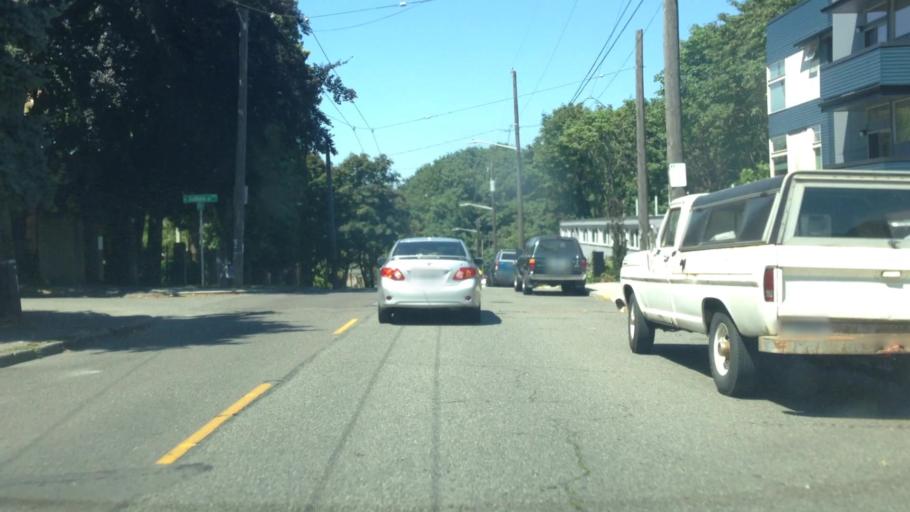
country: US
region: Washington
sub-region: King County
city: Seattle
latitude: 47.5913
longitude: -122.3149
